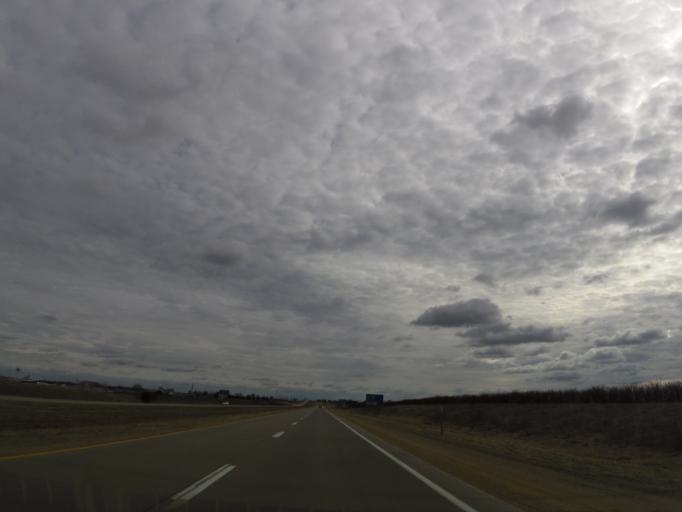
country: US
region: Iowa
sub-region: Chickasaw County
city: New Hampton
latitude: 43.0786
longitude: -92.3323
